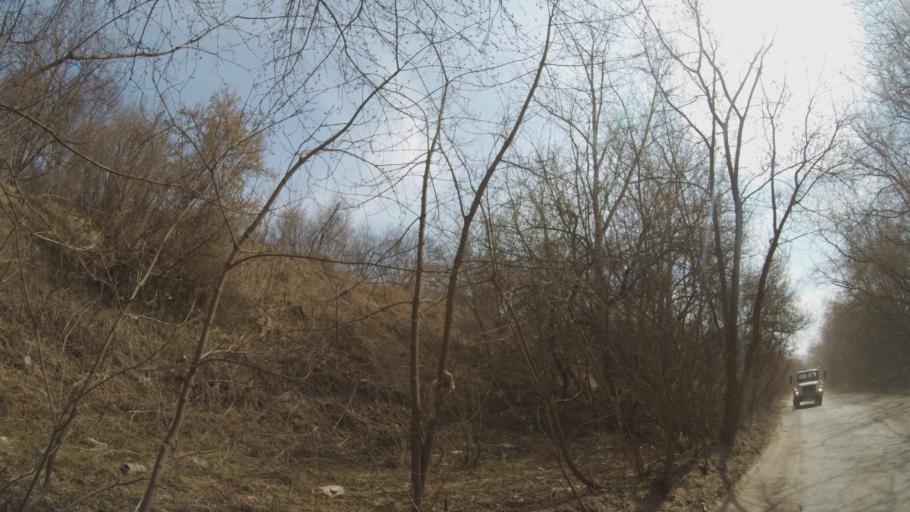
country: RU
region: Nizjnij Novgorod
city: Vyyezdnoye
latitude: 55.3891
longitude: 43.8095
